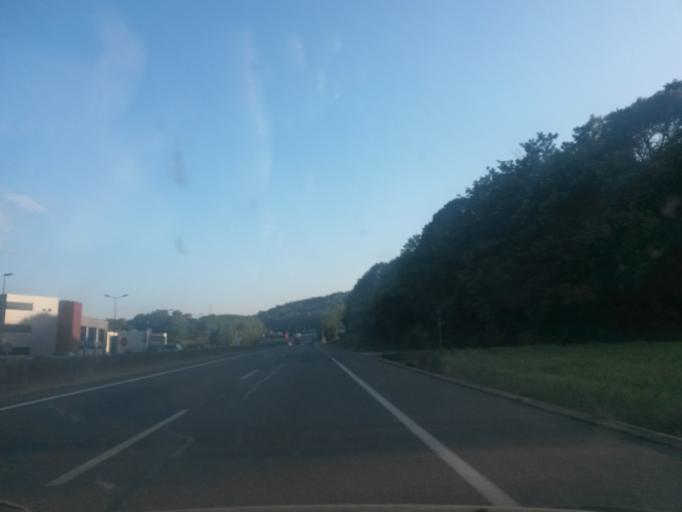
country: ES
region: Catalonia
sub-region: Provincia de Girona
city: Palol de Revardit
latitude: 42.0681
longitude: 2.8135
